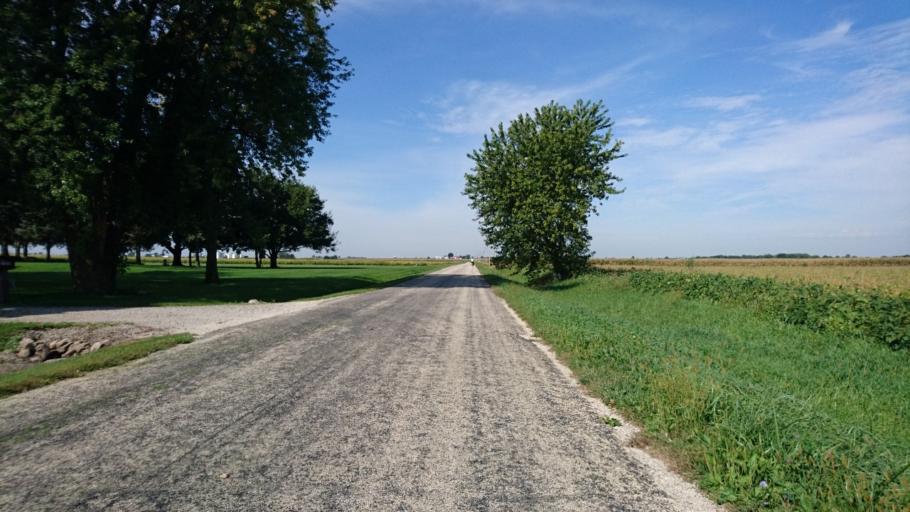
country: US
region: Illinois
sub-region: Will County
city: Manhattan
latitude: 41.4161
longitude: -88.0475
